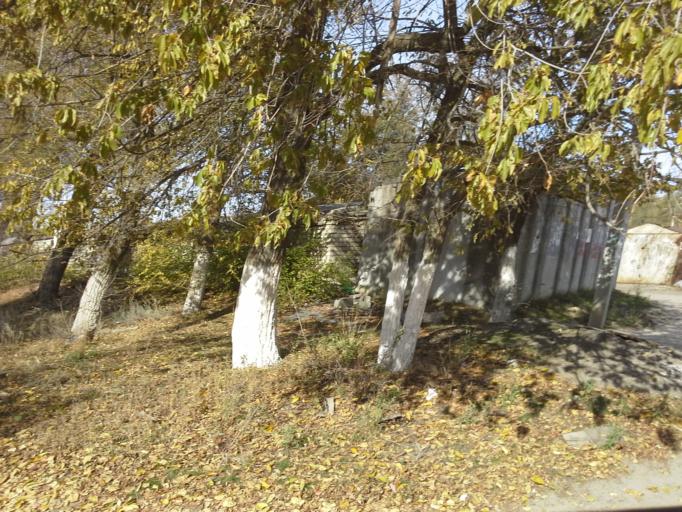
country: RU
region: Volgograd
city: Vodstroy
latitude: 48.8428
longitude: 44.6410
